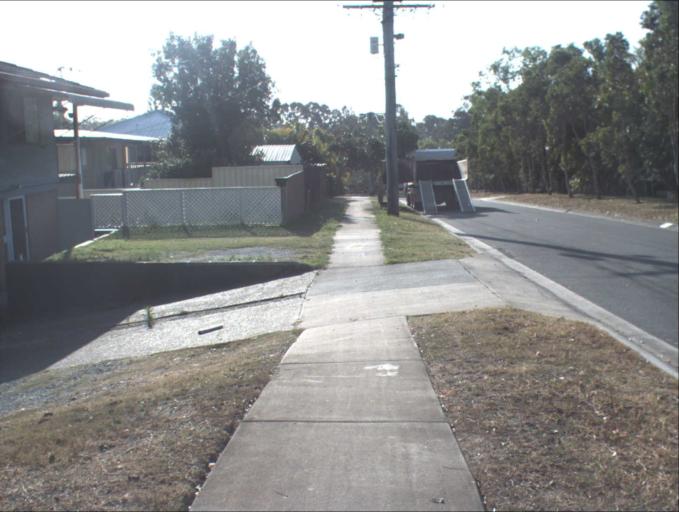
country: AU
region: Queensland
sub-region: Logan
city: Beenleigh
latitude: -27.6932
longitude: 153.1749
